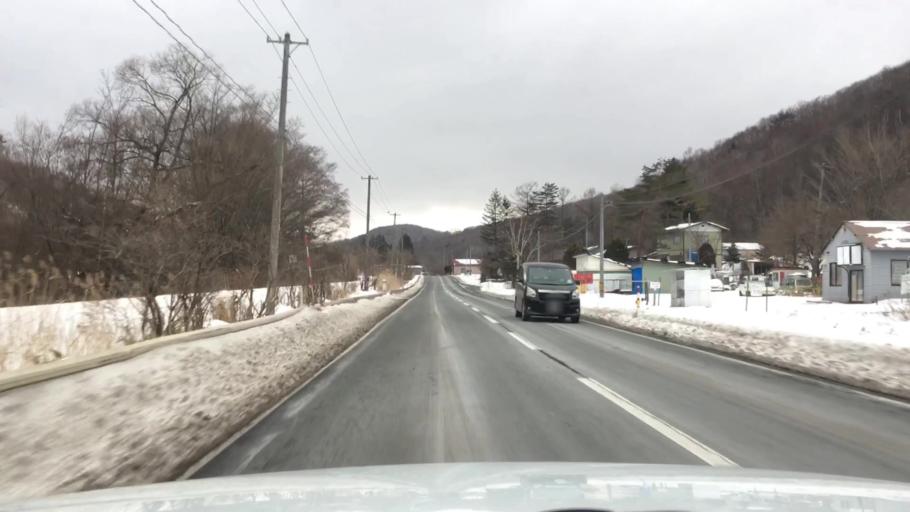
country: JP
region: Iwate
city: Morioka-shi
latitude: 39.6423
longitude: 141.4036
